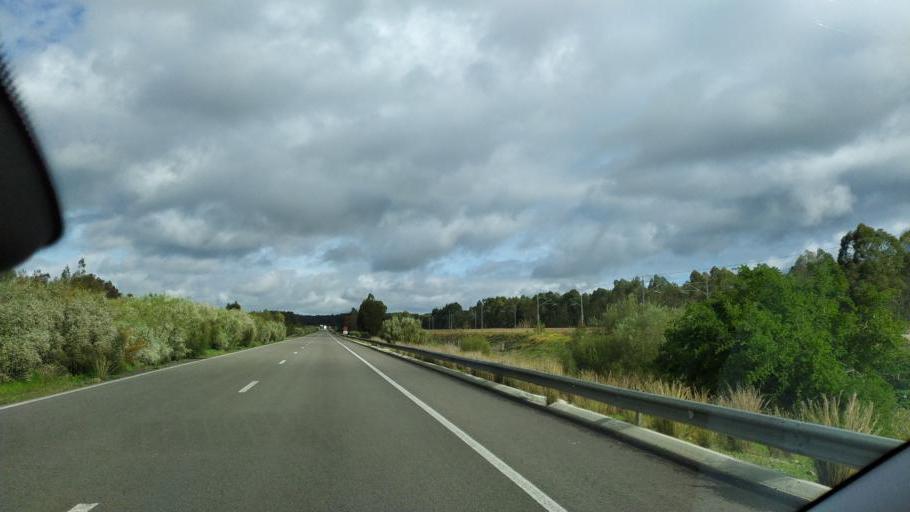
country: MA
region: Gharb-Chrarda-Beni Hssen
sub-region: Kenitra Province
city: Lalla Mimouna
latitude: 34.9077
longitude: -6.2071
